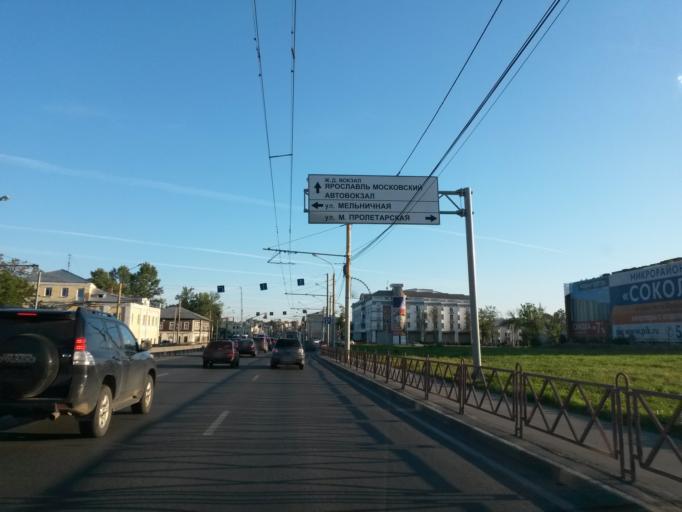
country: RU
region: Jaroslavl
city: Yaroslavl
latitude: 57.6139
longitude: 39.8833
